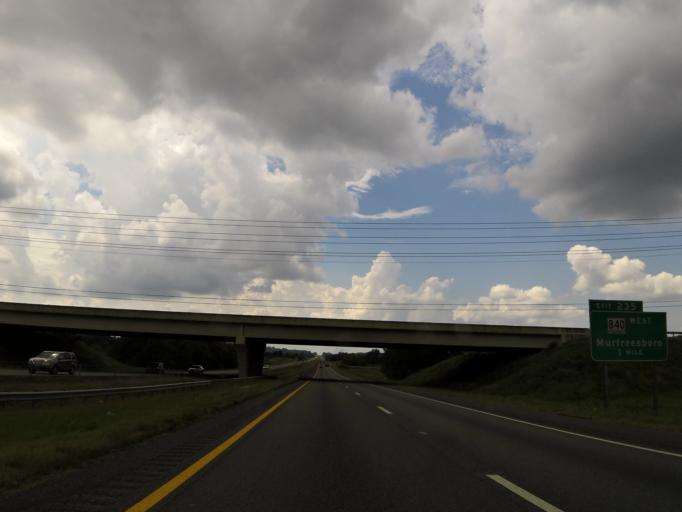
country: US
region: Tennessee
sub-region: Wilson County
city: Lebanon
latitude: 36.1831
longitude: -86.3250
